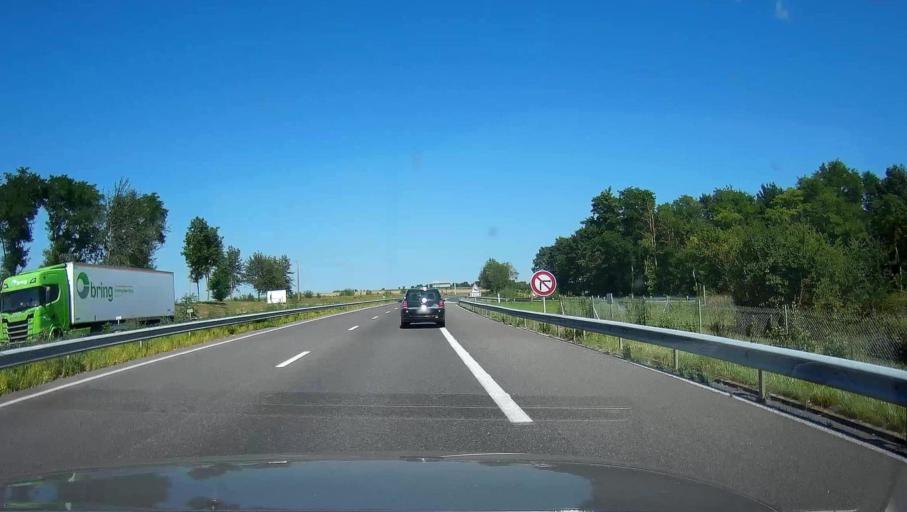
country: FR
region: Champagne-Ardenne
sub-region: Departement de la Marne
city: Fagnieres
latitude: 48.9716
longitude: 4.2835
